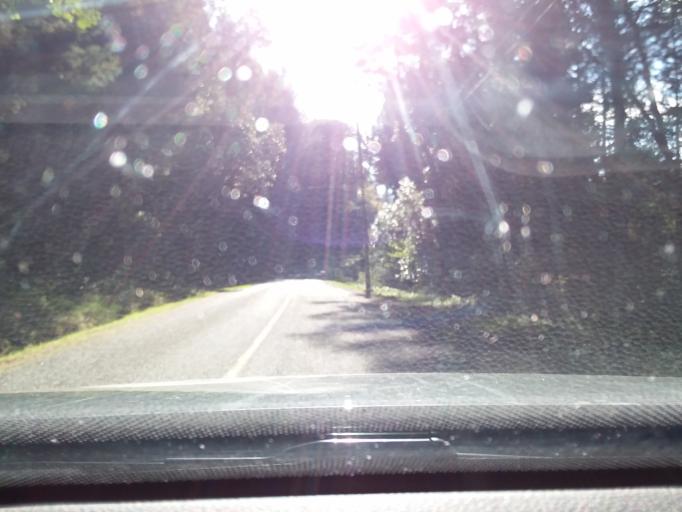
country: CA
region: British Columbia
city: North Cowichan
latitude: 48.9517
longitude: -123.5310
